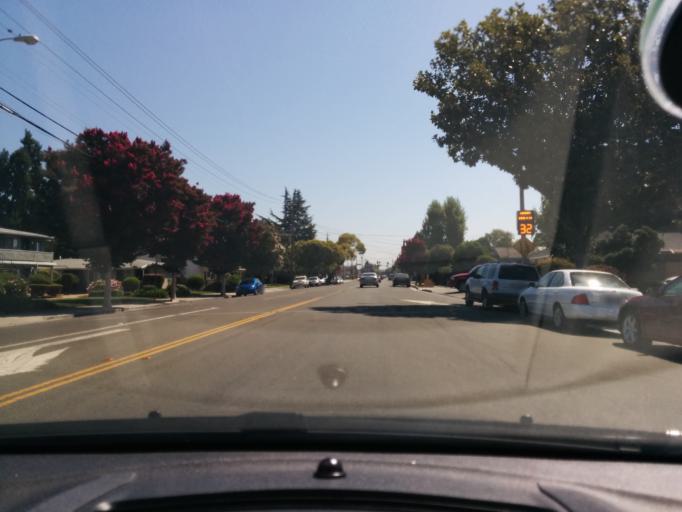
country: US
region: California
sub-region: Santa Clara County
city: Sunnyvale
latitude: 37.3890
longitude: -122.0286
